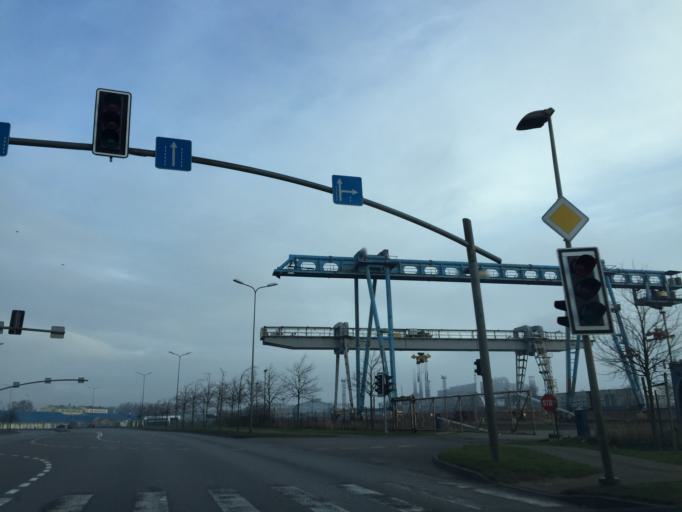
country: LV
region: Liepaja
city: Liepaja
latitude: 56.5195
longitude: 21.0271
